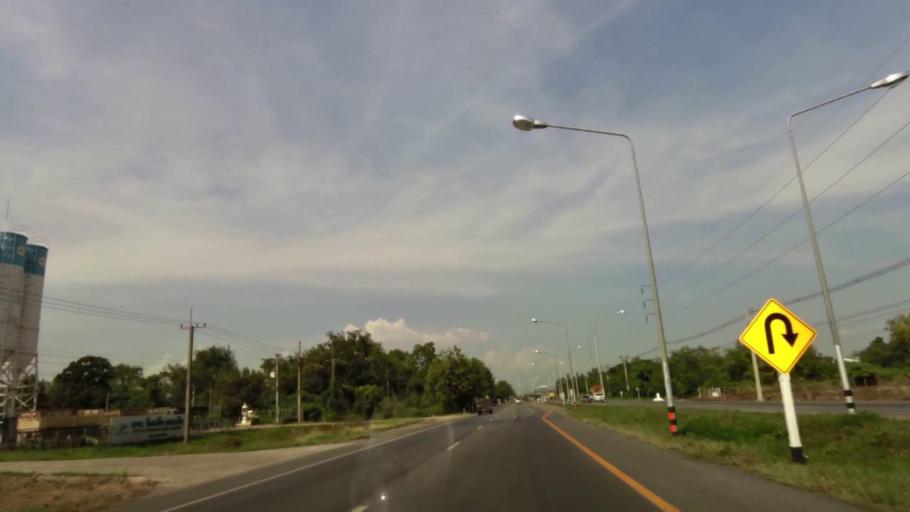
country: TH
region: Uttaradit
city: Uttaradit
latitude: 17.5761
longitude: 100.1475
